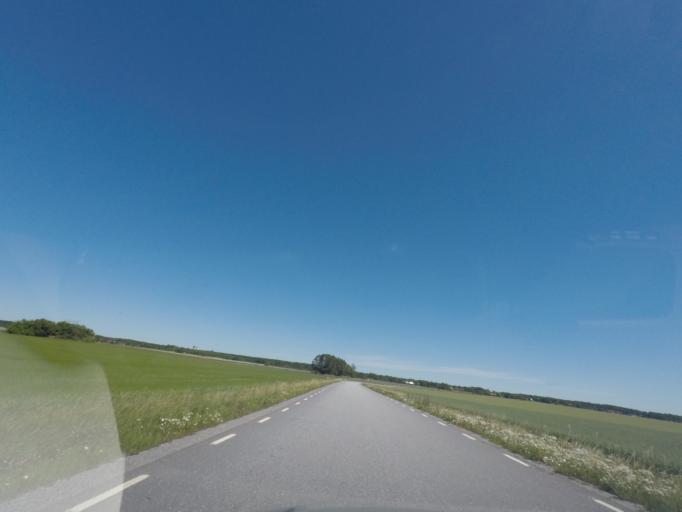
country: SE
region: Uppsala
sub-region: Enkopings Kommun
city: Enkoping
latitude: 59.7079
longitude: 17.0422
